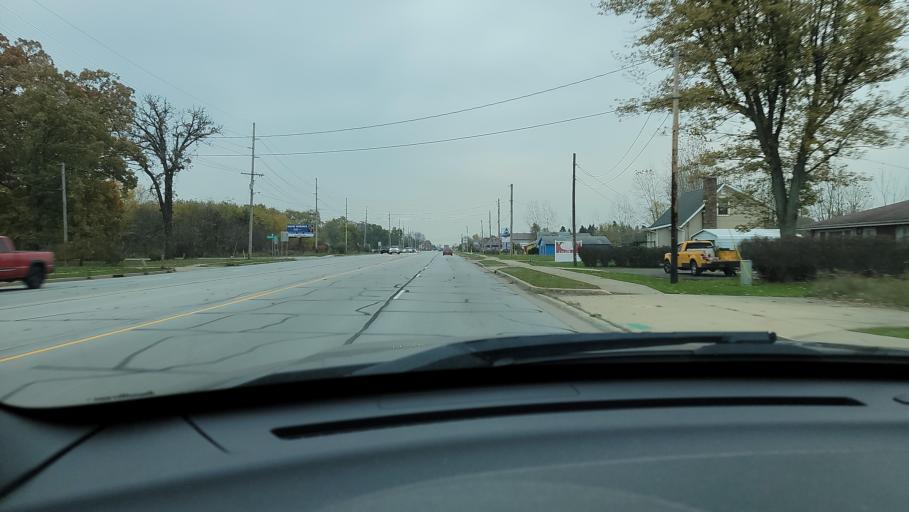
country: US
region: Indiana
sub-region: Porter County
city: Portage
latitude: 41.5505
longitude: -87.2060
